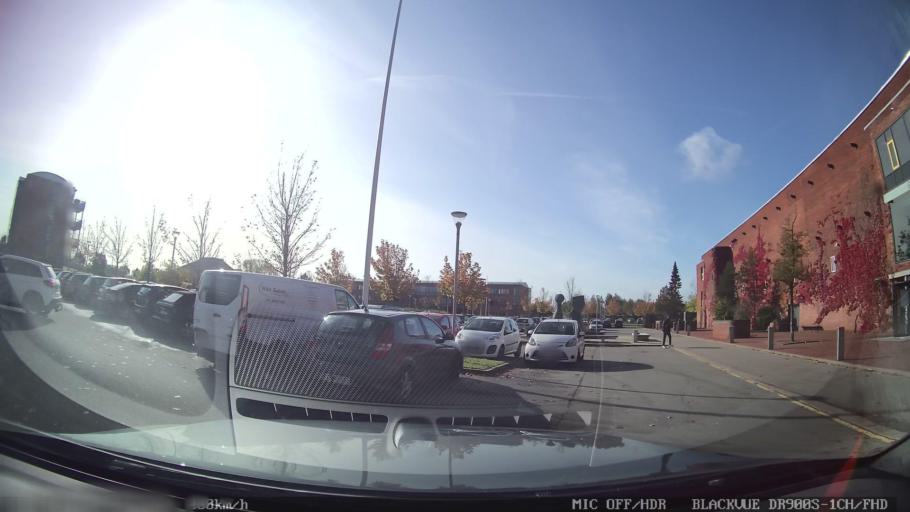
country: DK
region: Zealand
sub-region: Greve Kommune
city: Greve
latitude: 55.5830
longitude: 12.2907
